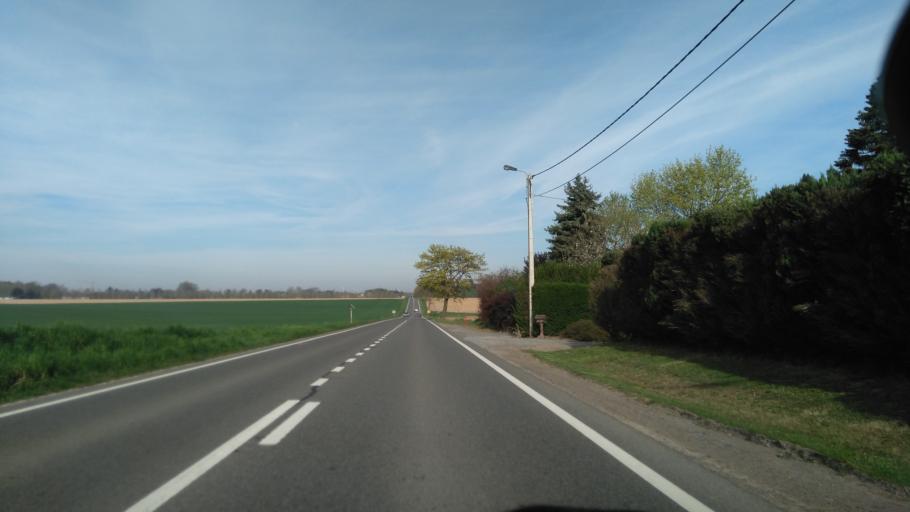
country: BE
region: Wallonia
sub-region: Province de Namur
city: Eghezee
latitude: 50.5879
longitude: 4.9334
